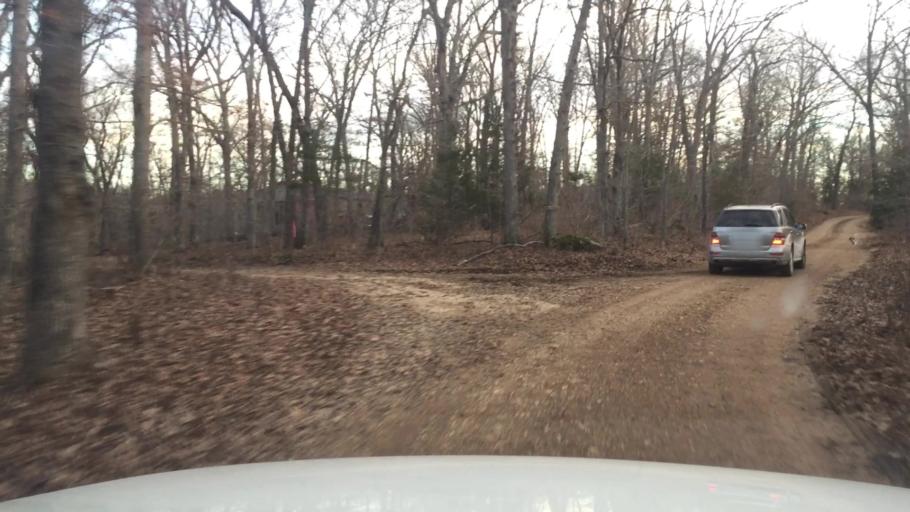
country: US
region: Missouri
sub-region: Camden County
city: Four Seasons
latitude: 38.3103
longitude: -92.7507
